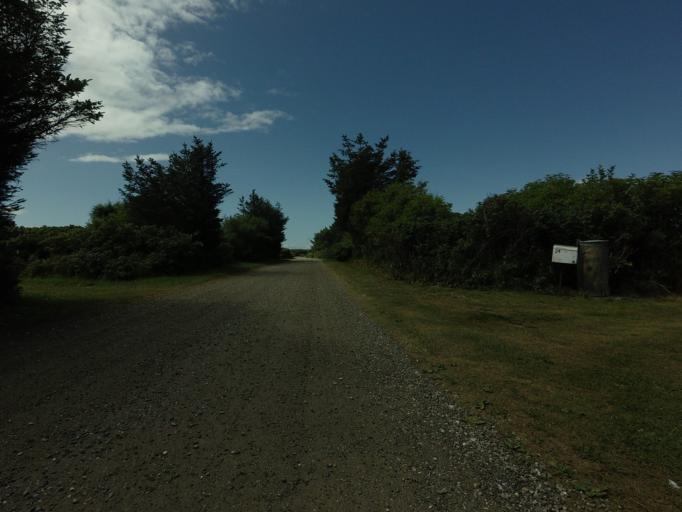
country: DK
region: North Denmark
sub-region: Jammerbugt Kommune
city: Pandrup
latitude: 57.3565
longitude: 9.7025
